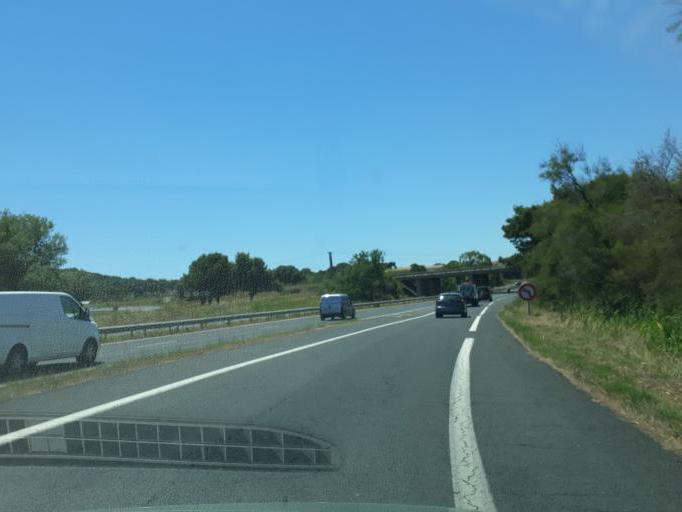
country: FR
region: Languedoc-Roussillon
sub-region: Departement de l'Herault
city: Le Cap d'Agde
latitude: 43.3083
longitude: 3.5102
